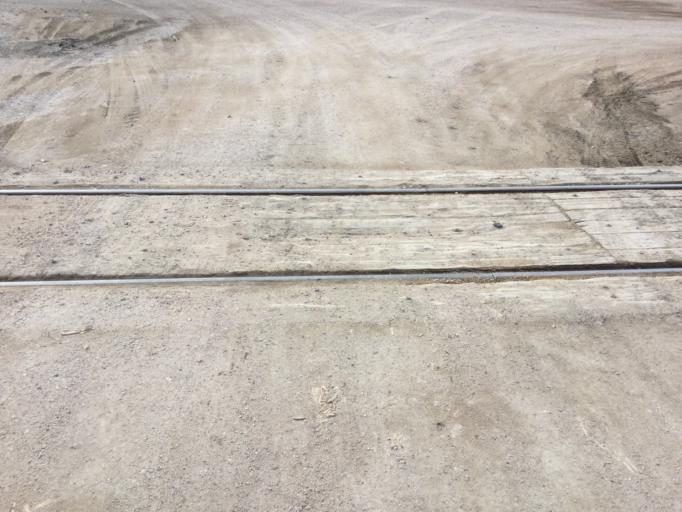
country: US
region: Kansas
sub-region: Lane County
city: Dighton
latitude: 38.4863
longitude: -100.4637
